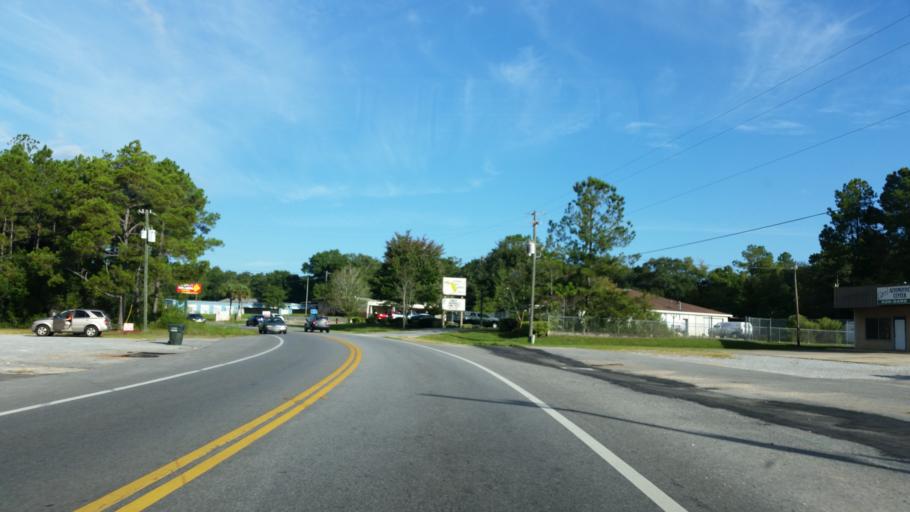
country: US
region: Florida
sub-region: Santa Rosa County
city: Milton
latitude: 30.6138
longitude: -87.0593
